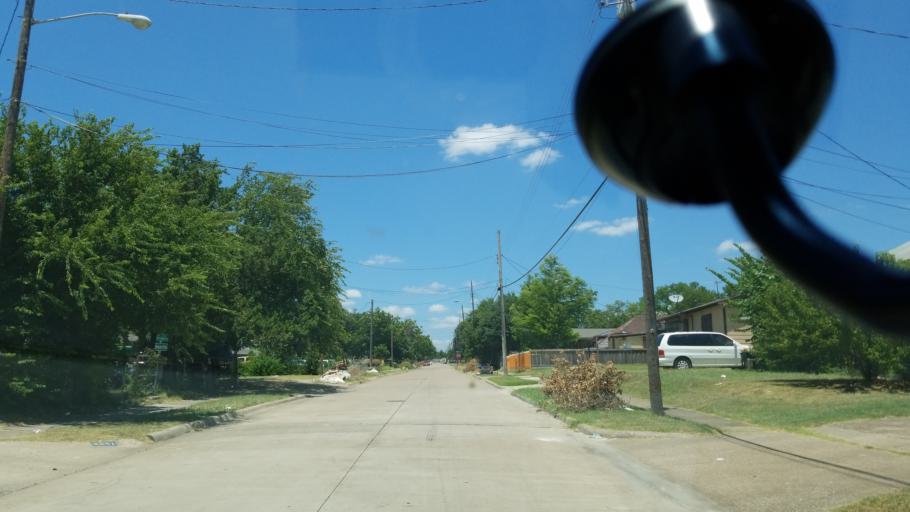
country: US
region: Texas
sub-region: Dallas County
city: Cockrell Hill
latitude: 32.6922
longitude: -96.8132
